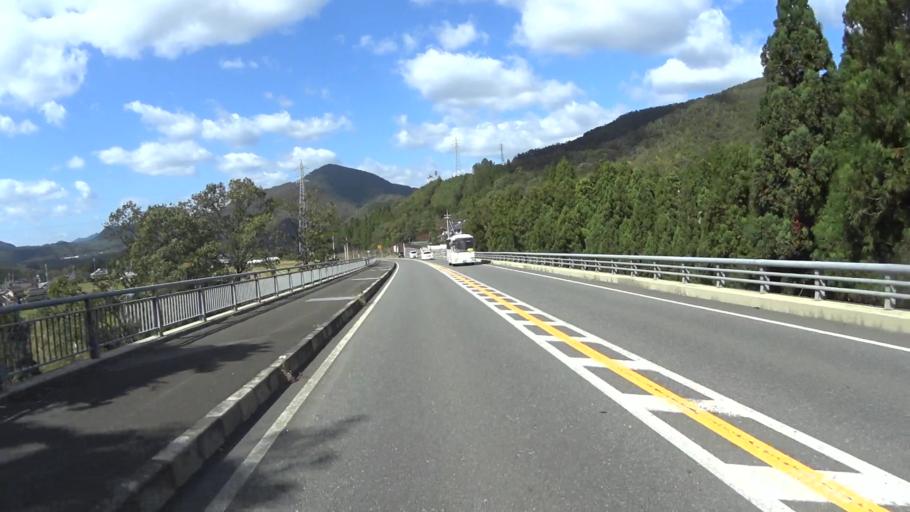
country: JP
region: Kyoto
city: Ayabe
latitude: 35.2162
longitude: 135.4287
